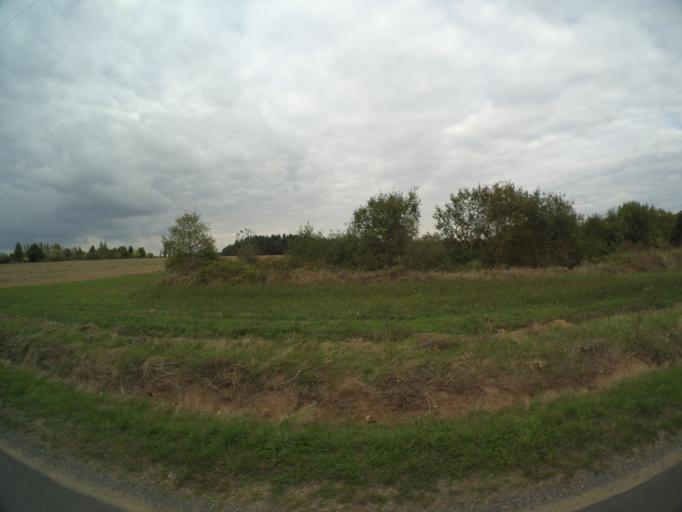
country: FR
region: Centre
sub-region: Departement d'Indre-et-Loire
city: Poce-sur-Cisse
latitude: 47.4985
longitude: 0.9810
